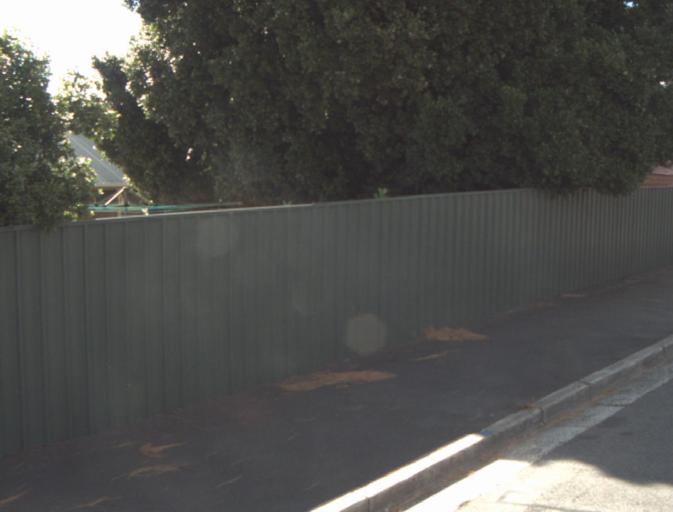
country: AU
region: Tasmania
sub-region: Launceston
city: East Launceston
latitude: -41.4449
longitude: 147.1557
